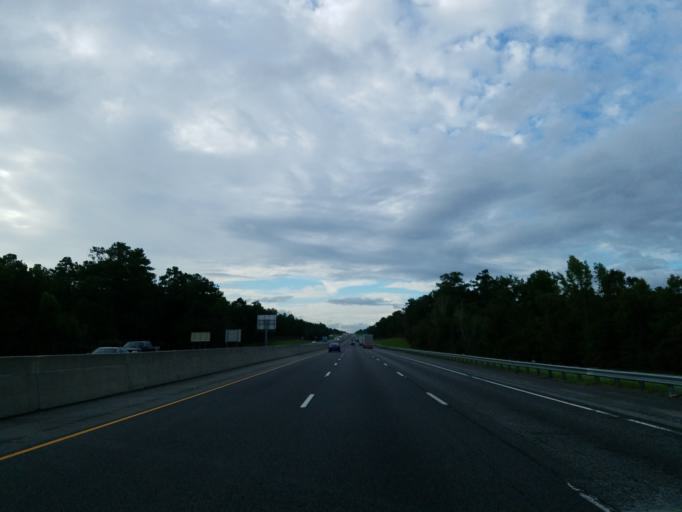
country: US
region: Georgia
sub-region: Lowndes County
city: Remerton
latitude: 30.9051
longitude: -83.3612
